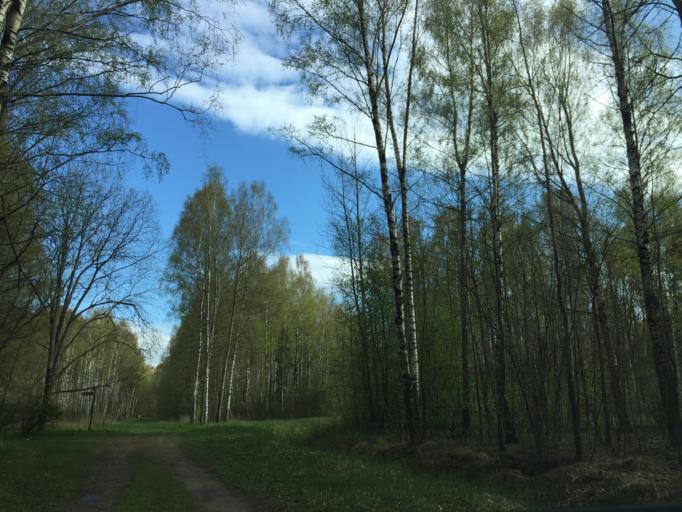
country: LV
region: Jelgava
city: Jelgava
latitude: 56.6246
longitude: 23.7412
